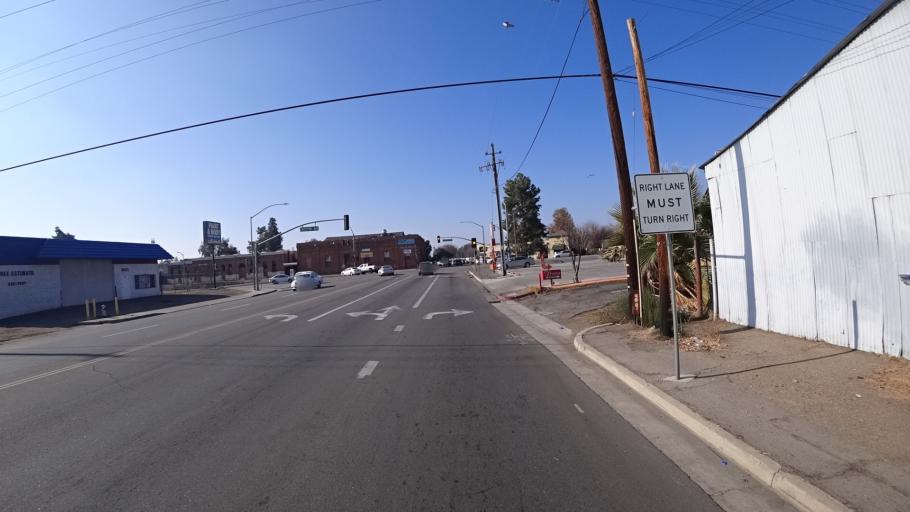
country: US
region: California
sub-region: Kern County
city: Bakersfield
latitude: 35.3906
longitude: -119.0180
